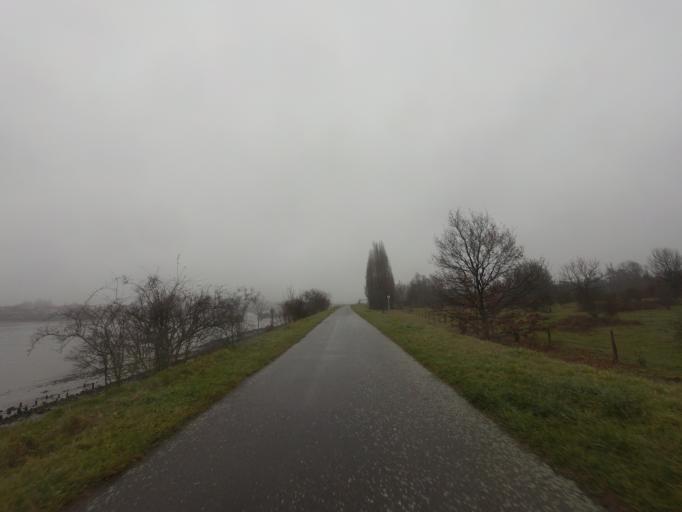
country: BE
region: Flanders
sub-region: Provincie Antwerpen
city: Hoboken
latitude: 51.1949
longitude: 4.3416
